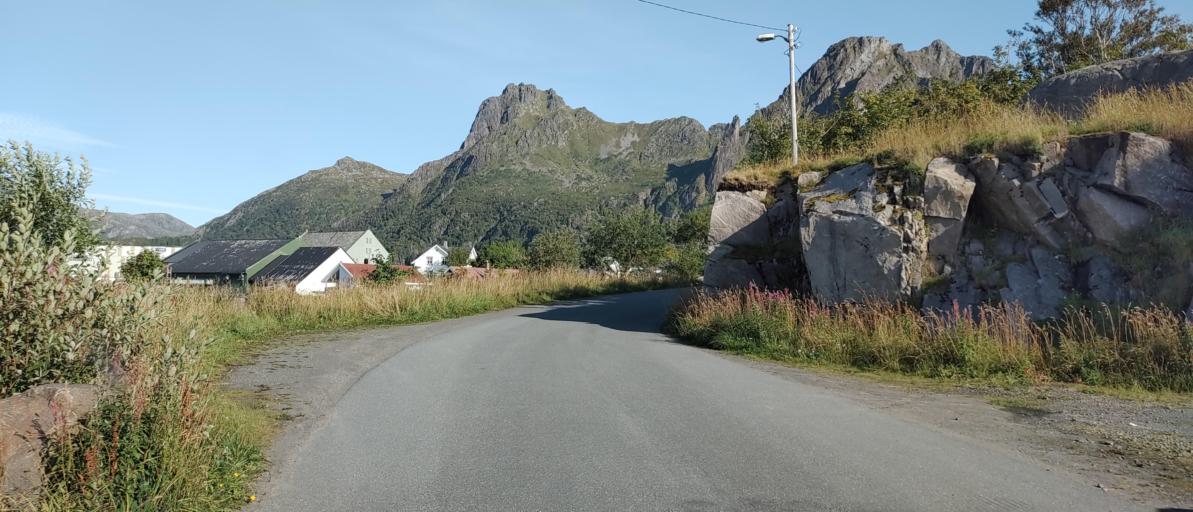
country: NO
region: Nordland
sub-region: Vagan
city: Svolvaer
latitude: 68.2316
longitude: 14.5778
